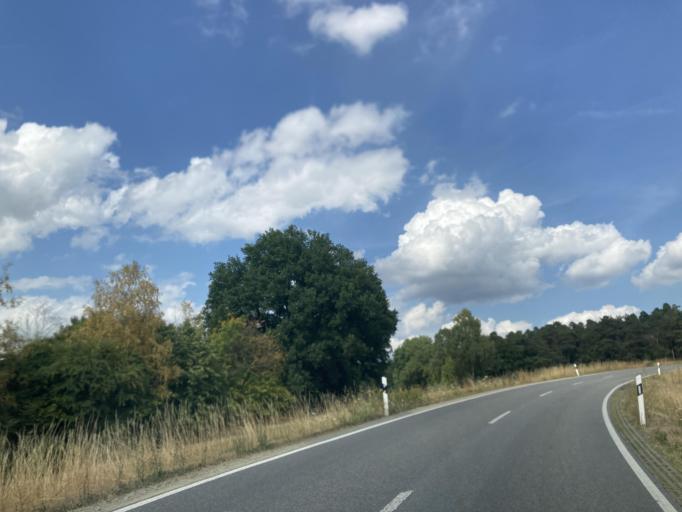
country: DE
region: Hesse
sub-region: Regierungsbezirk Kassel
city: Grossenluder
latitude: 50.5449
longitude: 9.5279
